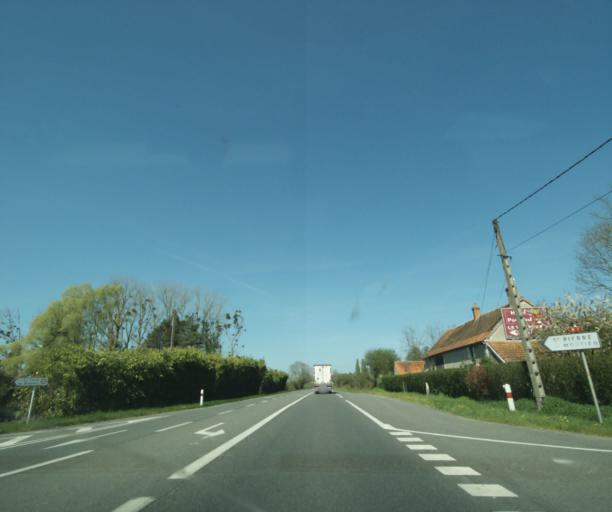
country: FR
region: Bourgogne
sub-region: Departement de la Nievre
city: Chantenay-Saint-Imbert
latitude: 46.7319
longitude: 3.1695
